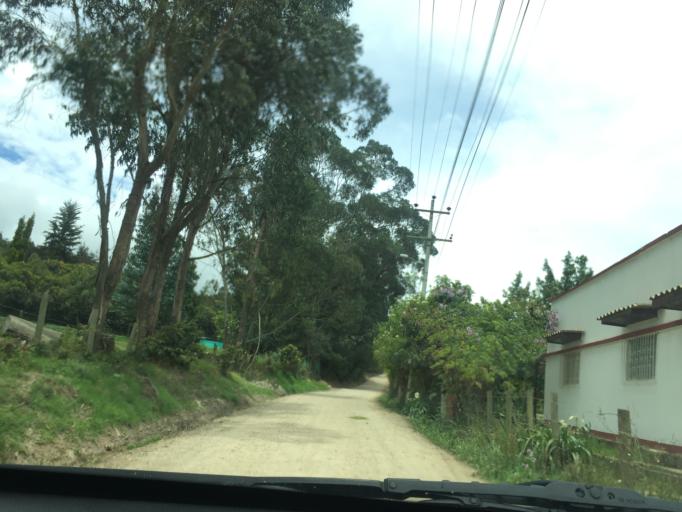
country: CO
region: Cundinamarca
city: El Rosal
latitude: 4.8728
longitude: -74.2531
